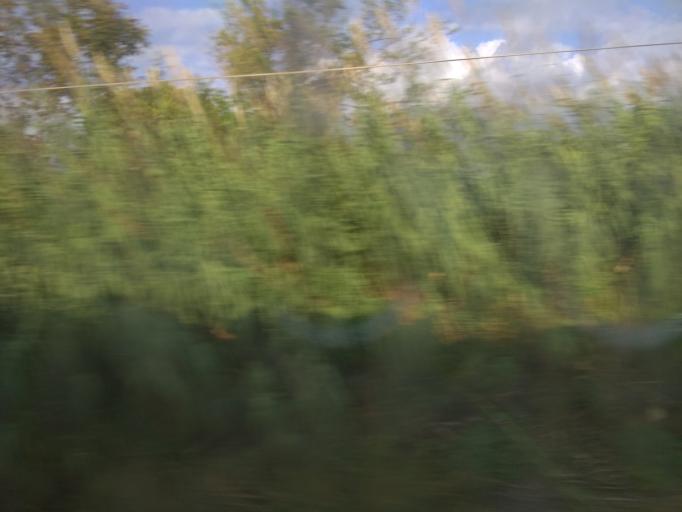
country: IT
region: Latium
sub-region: Citta metropolitana di Roma Capitale
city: Maccarese
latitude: 41.9064
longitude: 12.2100
